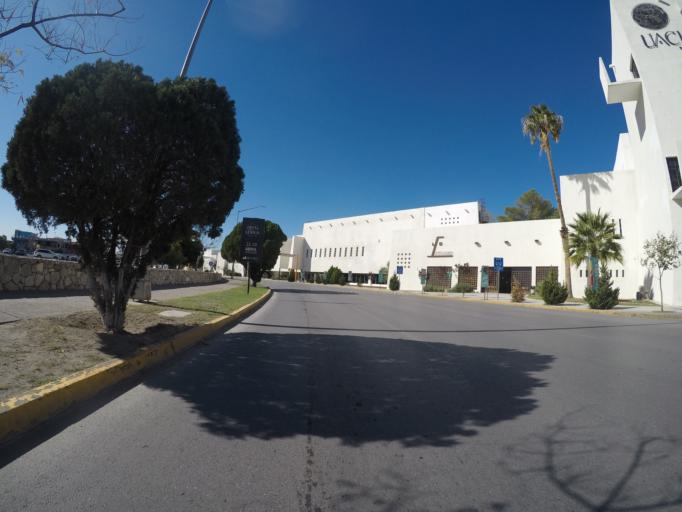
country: MX
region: Chihuahua
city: Ciudad Juarez
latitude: 31.7415
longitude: -106.4547
